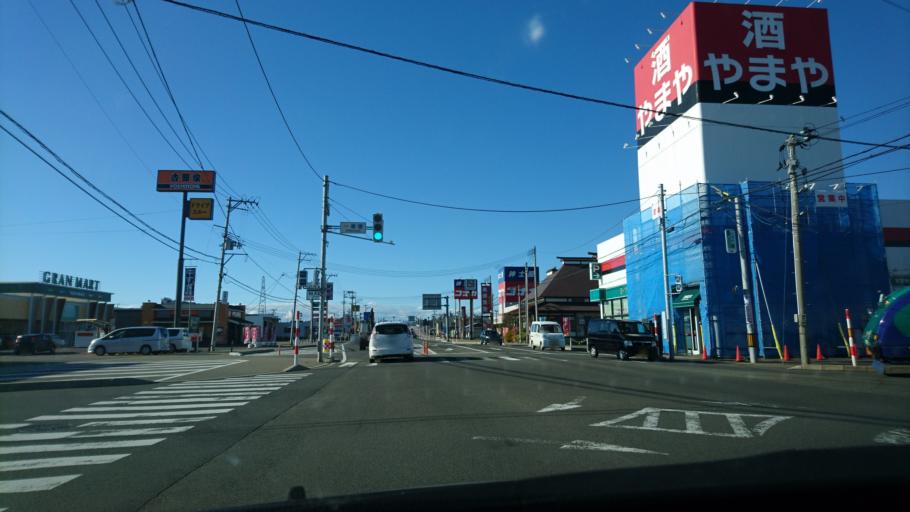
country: JP
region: Akita
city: Akita Shi
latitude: 39.3788
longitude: 140.0592
